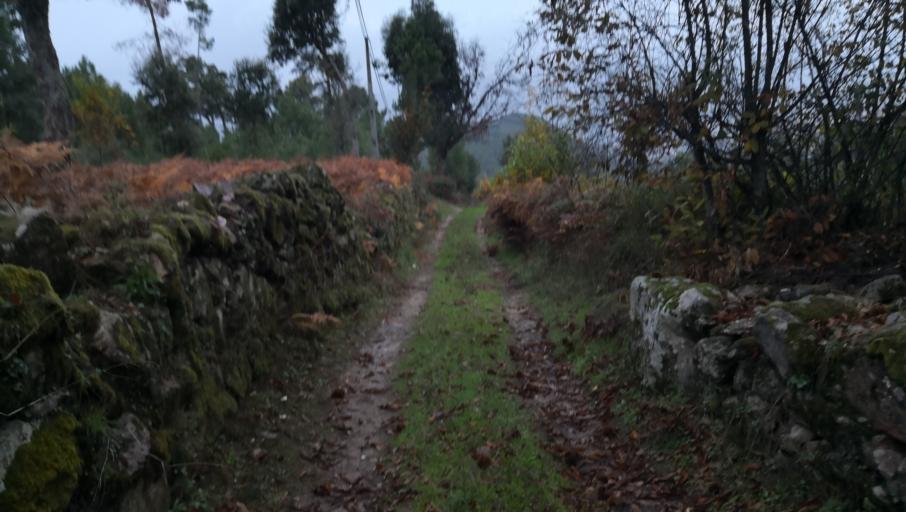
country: PT
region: Vila Real
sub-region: Vila Real
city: Vila Real
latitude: 41.2820
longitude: -7.7479
